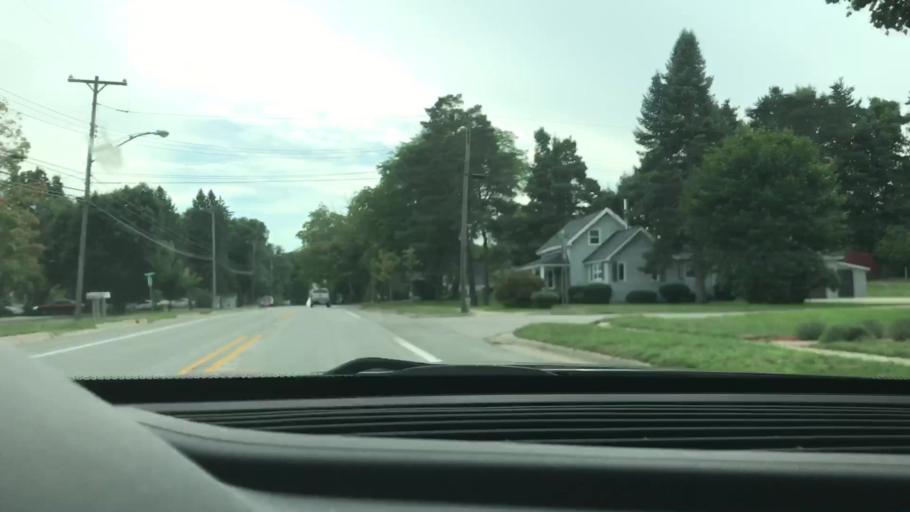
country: US
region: Michigan
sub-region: Antrim County
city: Bellaire
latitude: 44.9856
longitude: -85.2103
